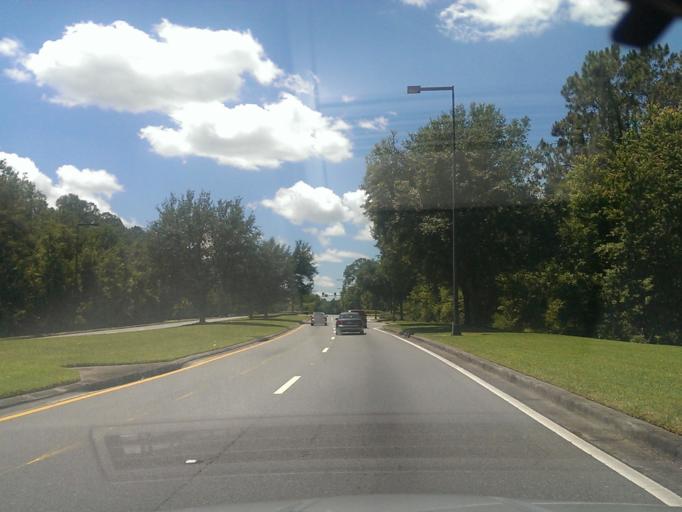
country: US
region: Florida
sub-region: Osceola County
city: Celebration
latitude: 28.3598
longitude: -81.5720
